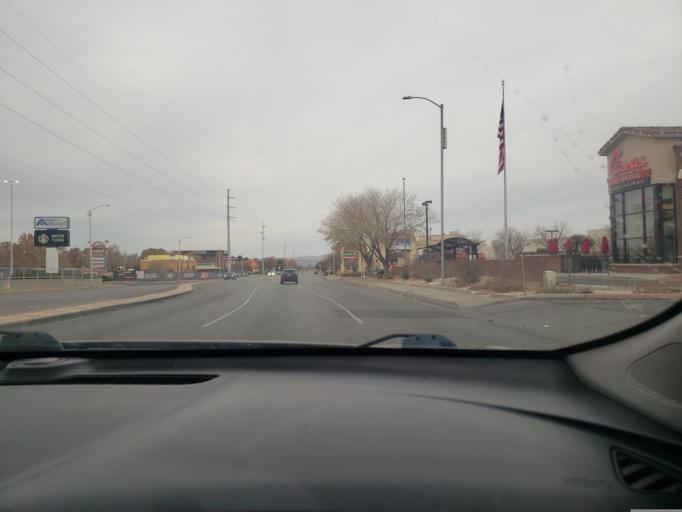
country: US
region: New Mexico
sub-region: Bernalillo County
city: North Valley
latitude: 35.1311
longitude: -106.5873
